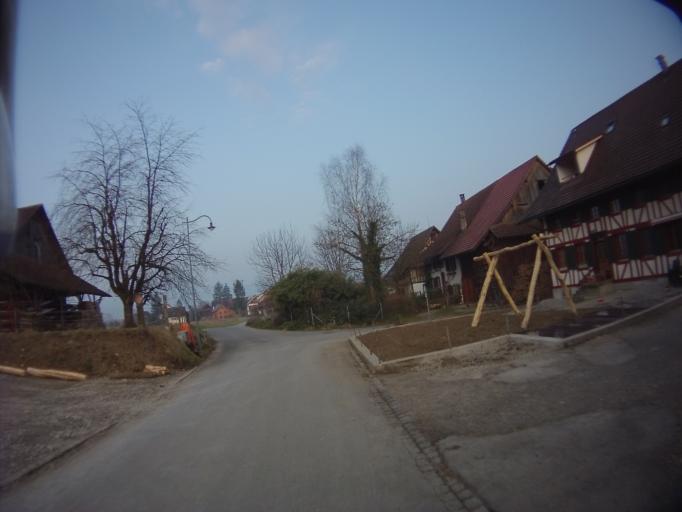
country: CH
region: Zurich
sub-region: Bezirk Affoltern
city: Obfelden / Toussen
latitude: 47.2343
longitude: 8.4322
